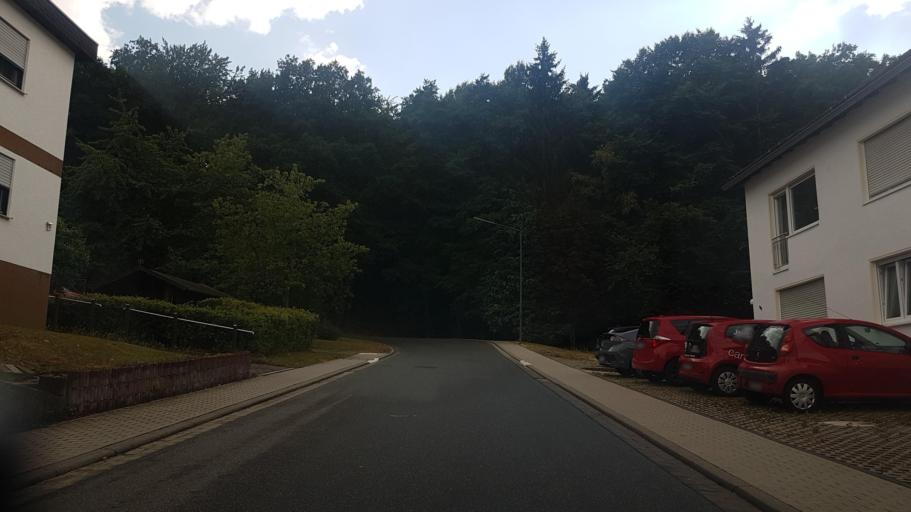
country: DE
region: Rheinland-Pfalz
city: Deuselbach
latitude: 49.7498
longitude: 7.0558
